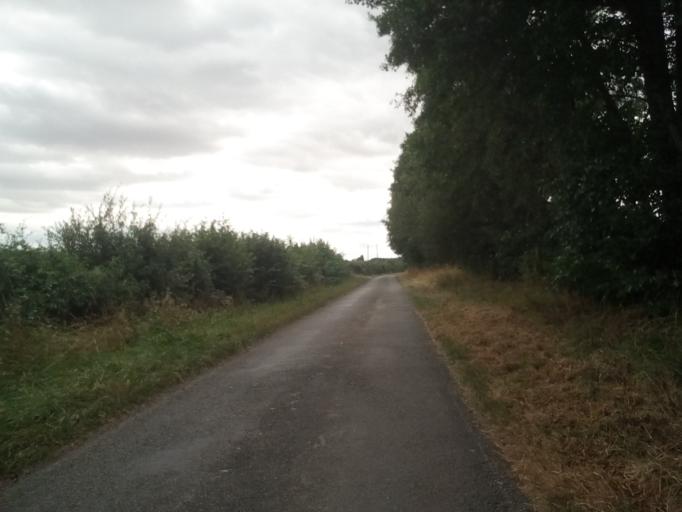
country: FR
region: Lower Normandy
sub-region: Departement du Calvados
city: Argences
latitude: 49.1554
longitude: -0.1571
